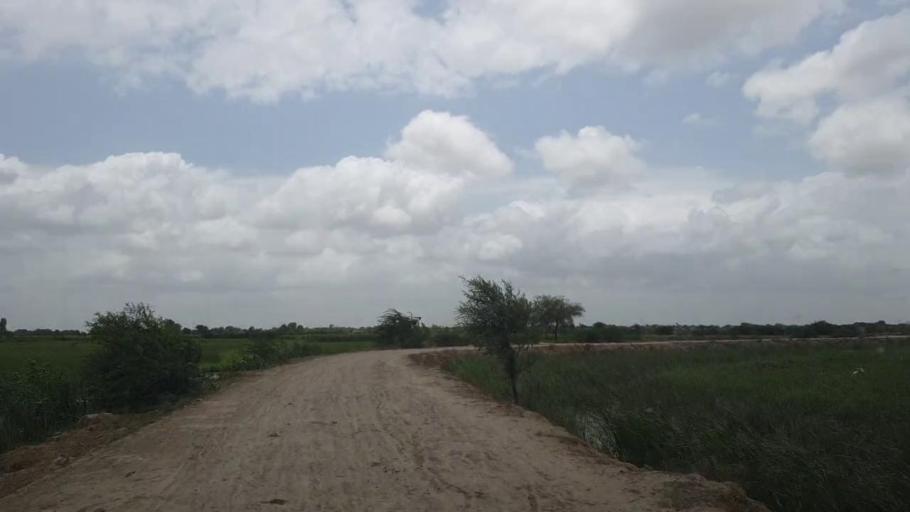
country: PK
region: Sindh
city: Badin
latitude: 24.6537
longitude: 68.9210
